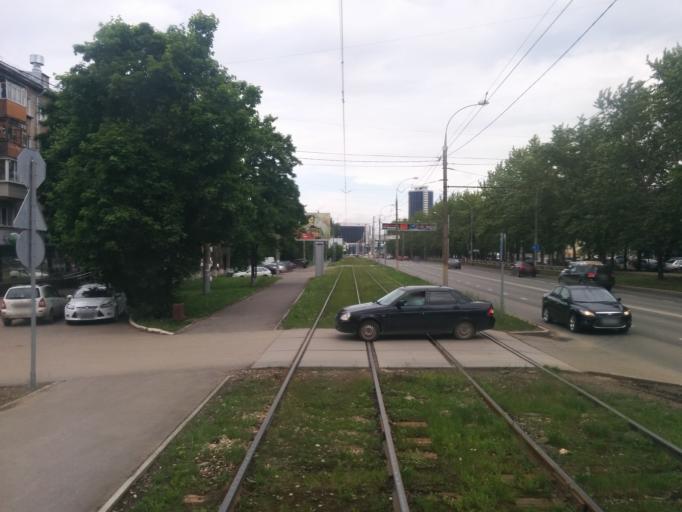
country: RU
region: Perm
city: Perm
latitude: 57.9997
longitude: 56.2869
